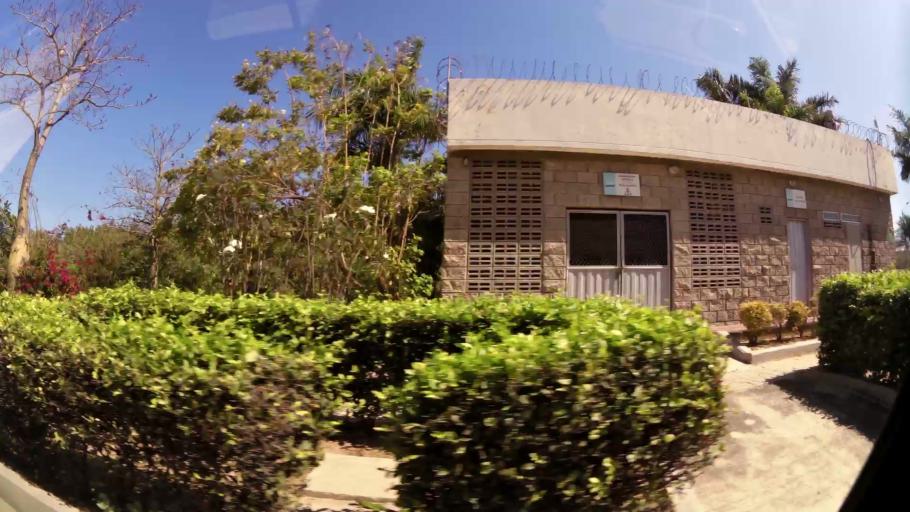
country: CO
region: Atlantico
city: Barranquilla
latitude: 11.0203
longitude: -74.8392
